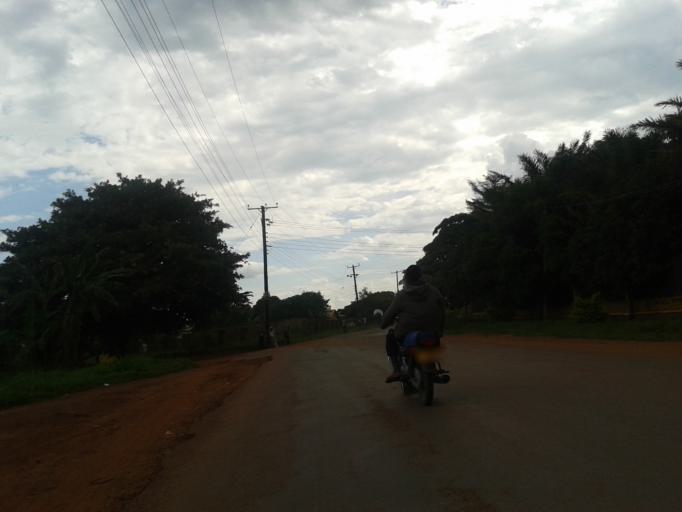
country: UG
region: Northern Region
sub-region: Gulu District
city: Gulu
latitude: 2.7794
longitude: 32.3003
